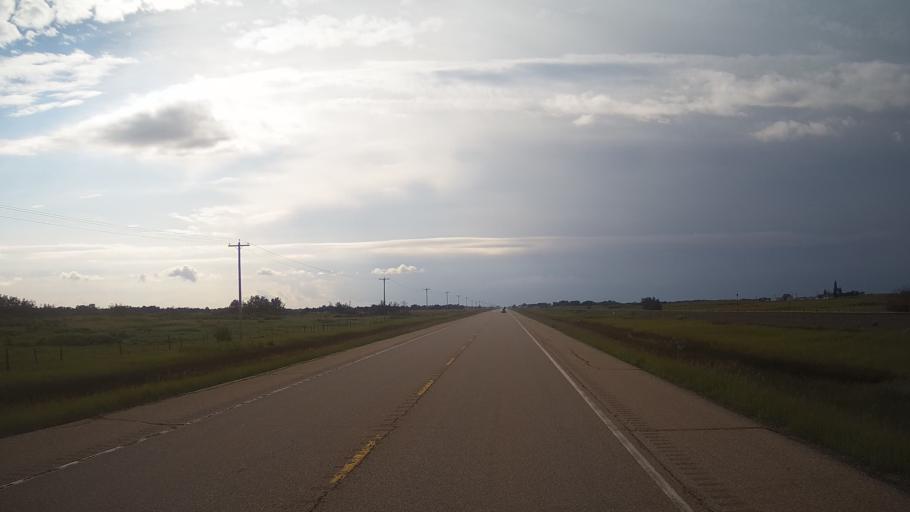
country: CA
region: Alberta
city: Viking
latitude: 53.1435
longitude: -111.9472
